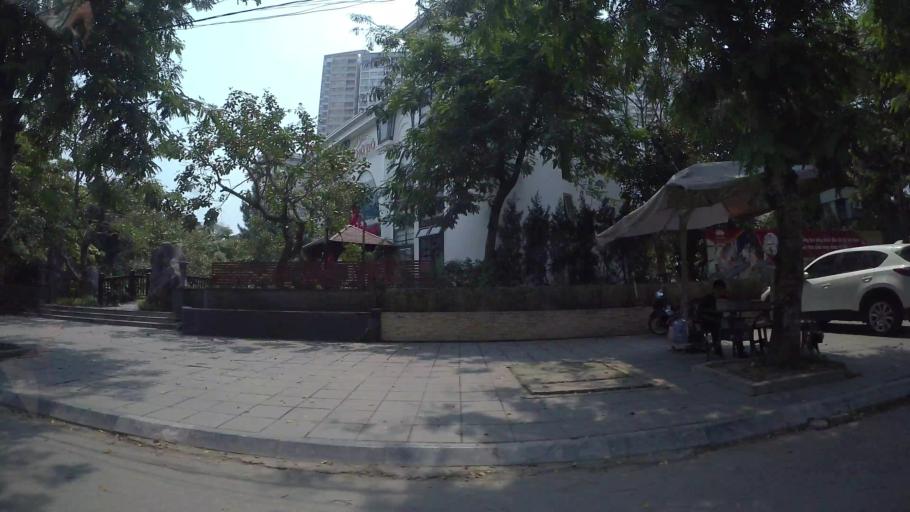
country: VN
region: Ha Noi
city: Thanh Xuan
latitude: 21.0062
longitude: 105.8007
